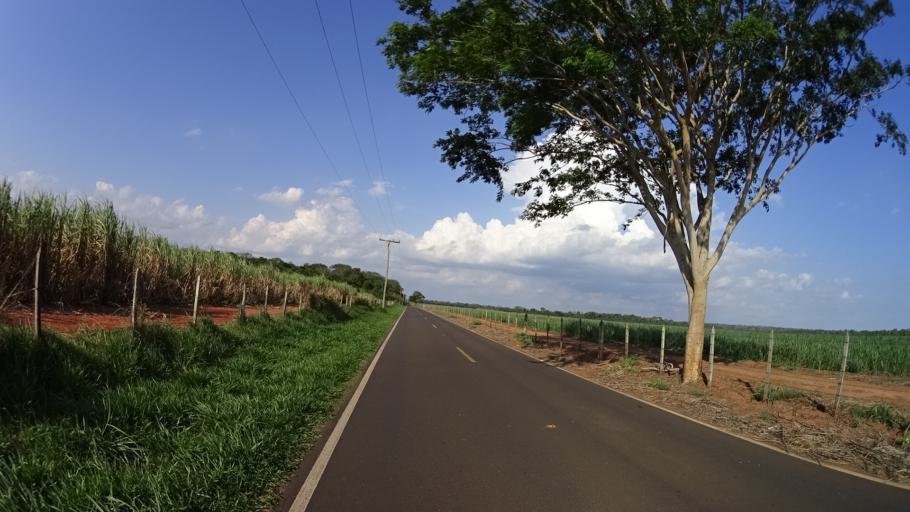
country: BR
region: Sao Paulo
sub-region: Urupes
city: Urupes
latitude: -21.3885
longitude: -49.5003
